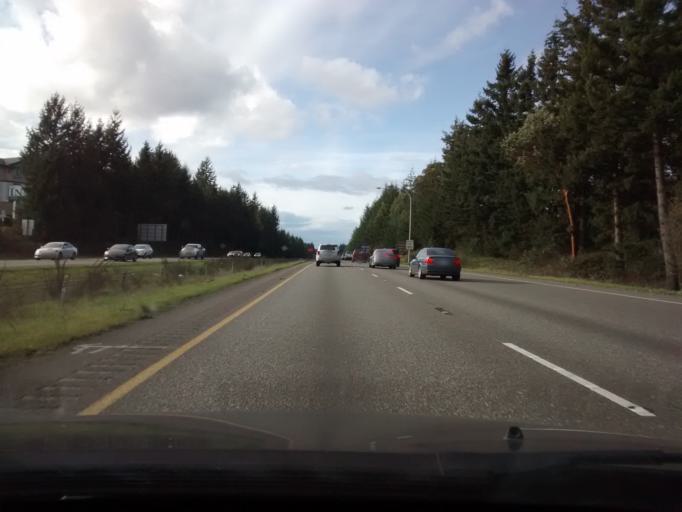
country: US
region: Washington
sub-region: Pierce County
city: Gig Harbor
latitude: 47.3094
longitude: -122.5800
